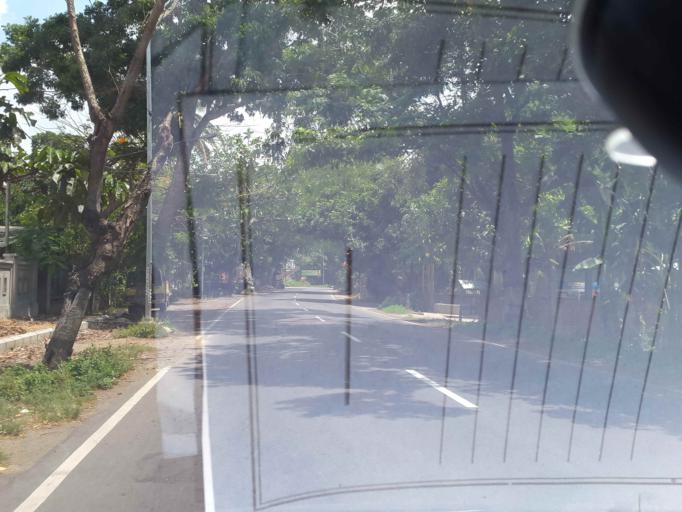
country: ID
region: West Nusa Tenggara
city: Jelateng Timur
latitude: -8.7095
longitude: 116.0776
